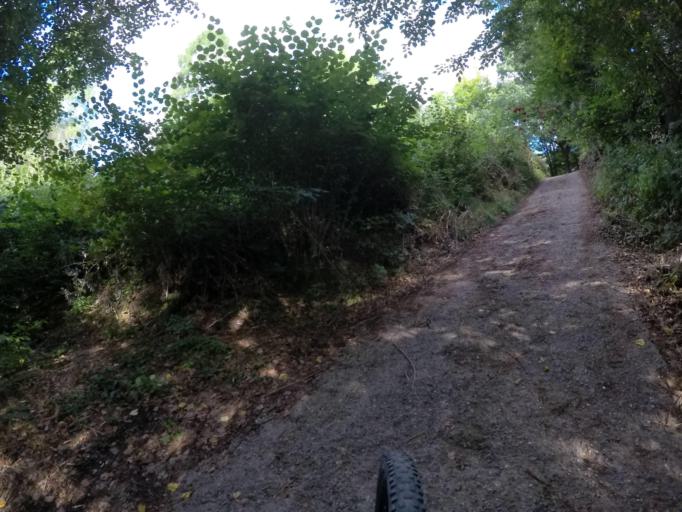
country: IT
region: Friuli Venezia Giulia
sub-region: Provincia di Udine
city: Paularo
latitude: 46.5410
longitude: 13.1122
